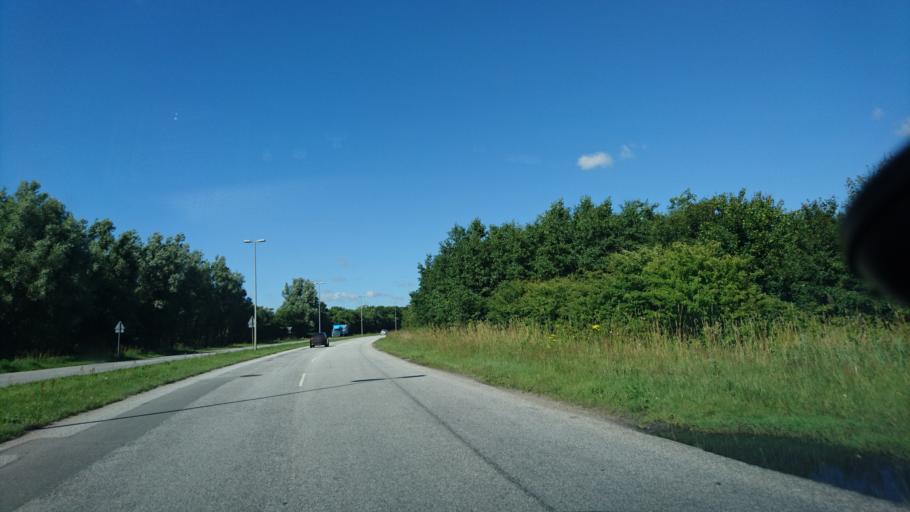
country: DK
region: North Denmark
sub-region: Alborg Kommune
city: Gistrup
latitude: 57.0216
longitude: 10.0051
